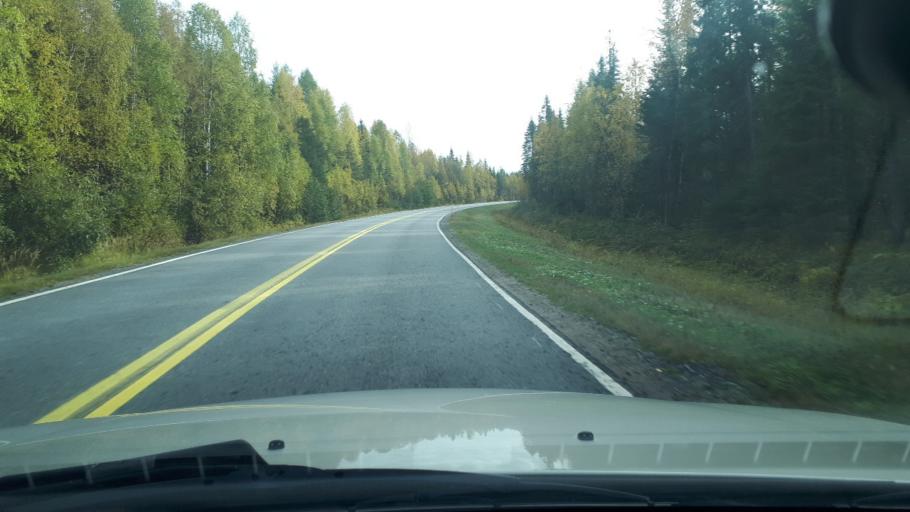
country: FI
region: Lapland
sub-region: Rovaniemi
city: Ranua
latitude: 65.9681
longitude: 26.0119
